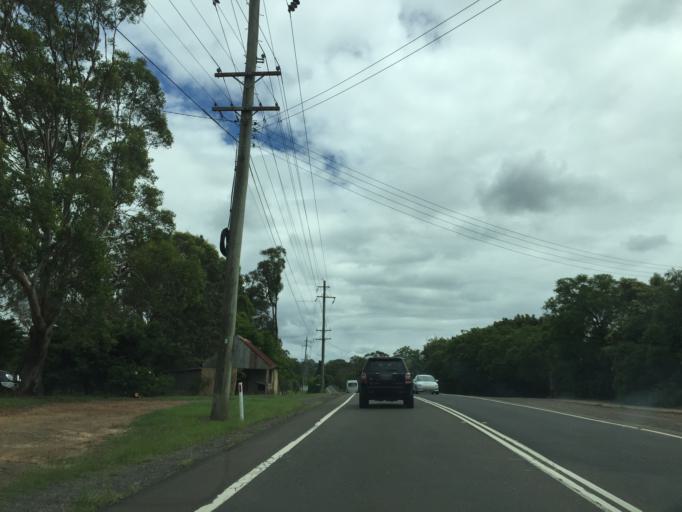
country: AU
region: New South Wales
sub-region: Hawkesbury
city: Richmond
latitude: -33.5643
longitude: 150.7035
